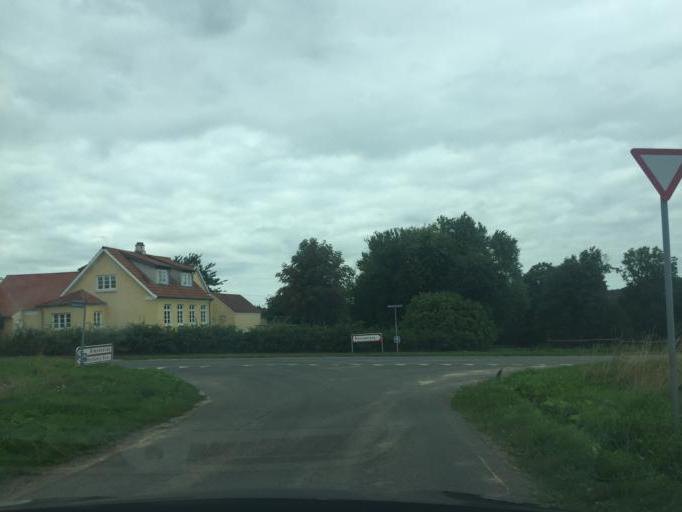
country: DK
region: South Denmark
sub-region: Assens Kommune
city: Tommerup Stationsby
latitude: 55.3771
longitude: 10.2187
